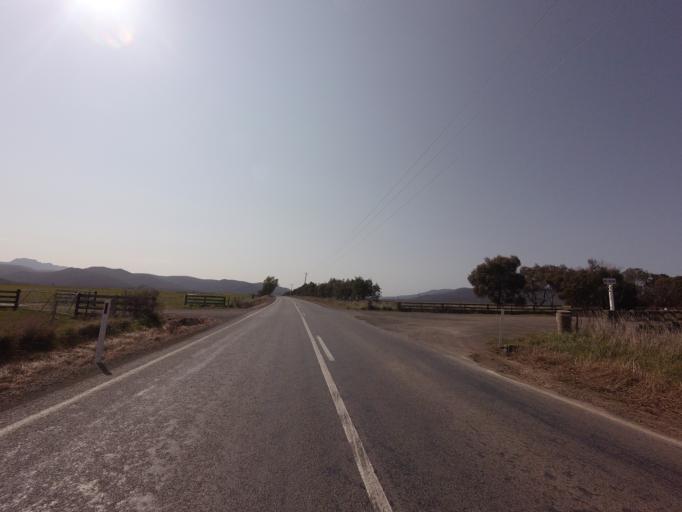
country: AU
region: Tasmania
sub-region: Northern Midlands
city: Evandale
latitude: -41.7950
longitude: 147.7083
